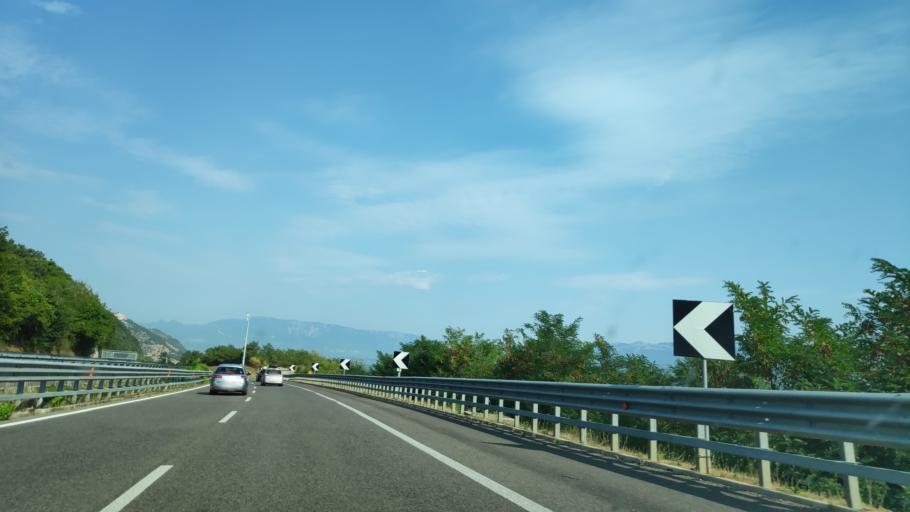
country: IT
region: Campania
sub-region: Provincia di Salerno
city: Petina
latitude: 40.5640
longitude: 15.3806
